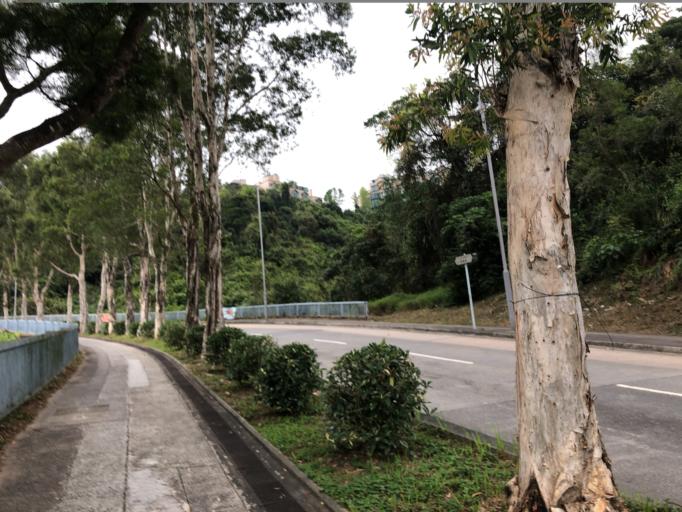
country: HK
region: Tai Po
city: Tai Po
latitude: 22.4635
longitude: 114.1925
